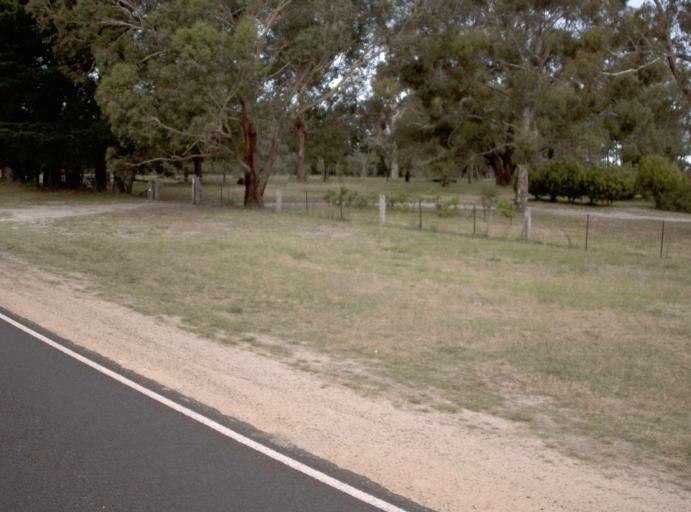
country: AU
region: Victoria
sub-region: Wellington
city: Sale
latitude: -38.2172
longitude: 147.1201
